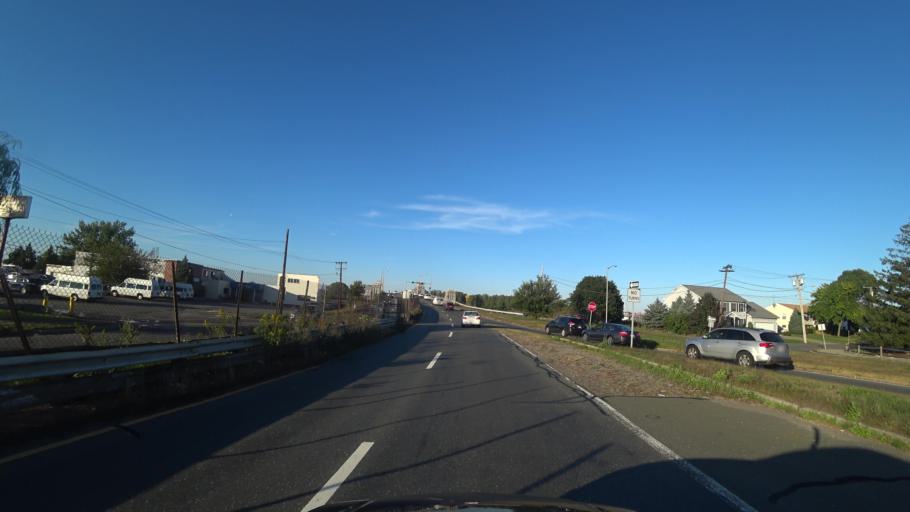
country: US
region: Massachusetts
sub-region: Essex County
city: Lynn
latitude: 42.4413
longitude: -70.9672
